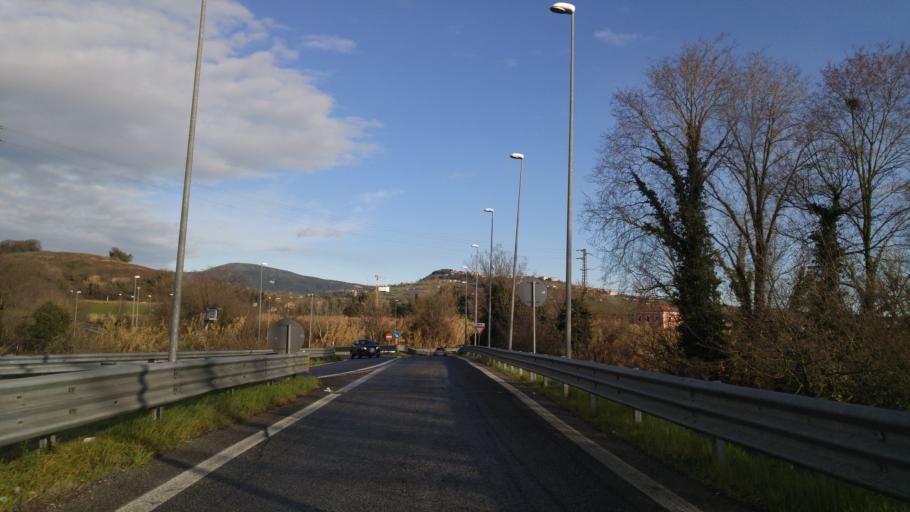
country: IT
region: The Marches
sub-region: Provincia di Ancona
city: San Biagio
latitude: 43.5327
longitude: 13.5135
